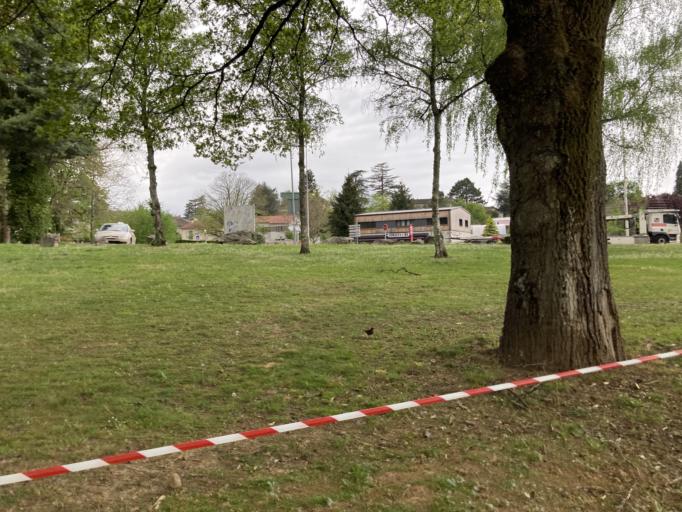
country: FR
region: Limousin
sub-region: Departement de la Haute-Vienne
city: Isle
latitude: 45.8180
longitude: 1.2301
